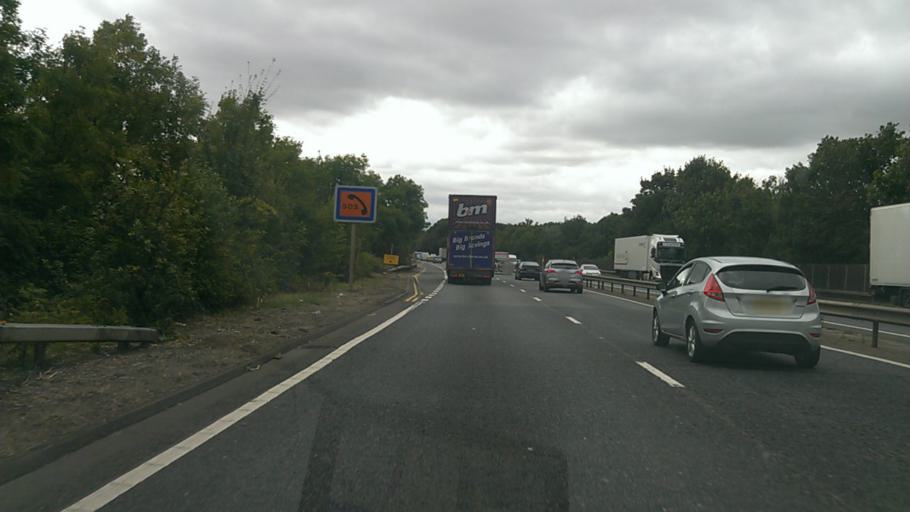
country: GB
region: England
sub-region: Cambridgeshire
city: Huntingdon
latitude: 52.3341
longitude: -0.1965
